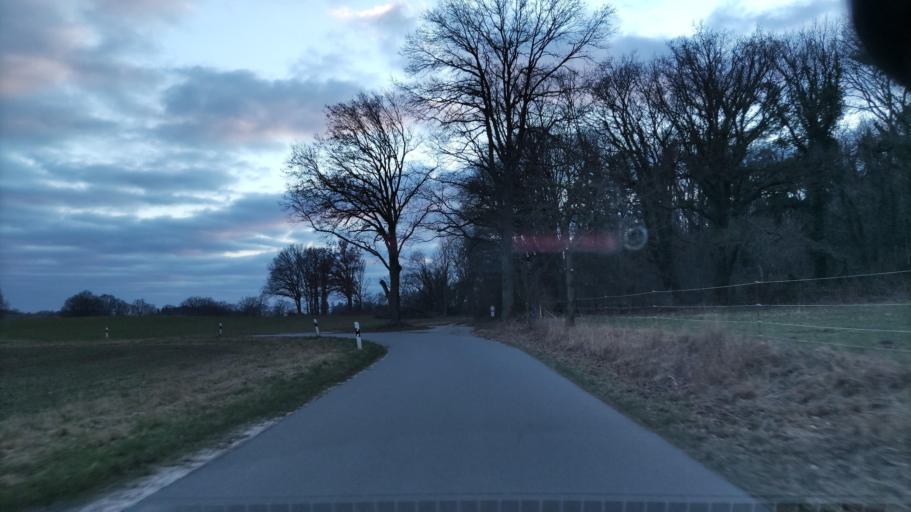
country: DE
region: Lower Saxony
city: Natendorf
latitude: 53.0781
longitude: 10.4413
